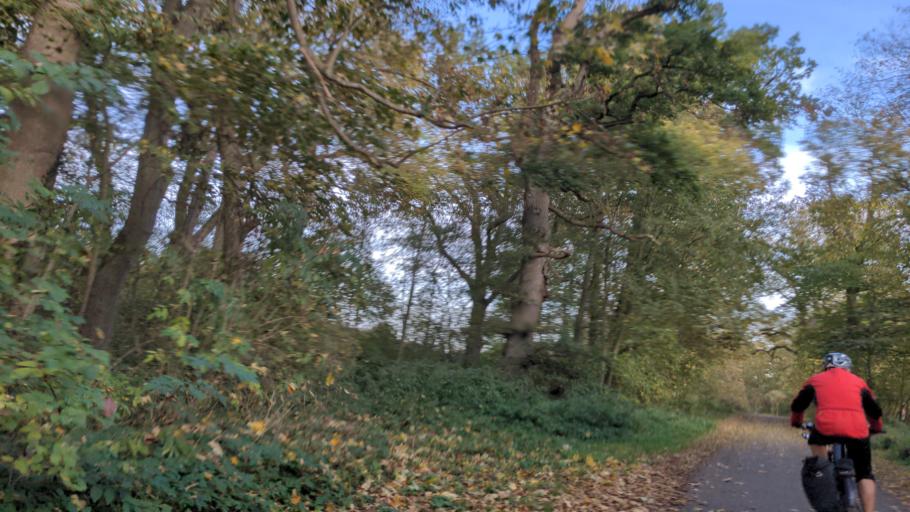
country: DE
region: Schleswig-Holstein
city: Neustadt in Holstein
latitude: 54.1305
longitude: 10.7795
